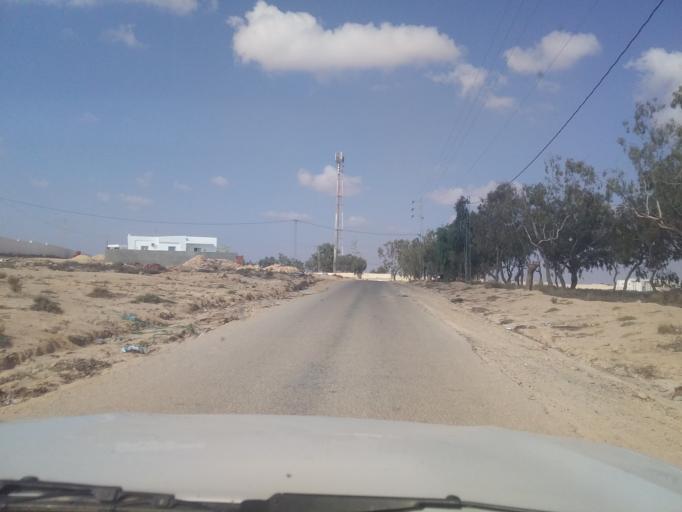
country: TN
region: Qabis
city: Gabes
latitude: 33.6313
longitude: 10.2759
